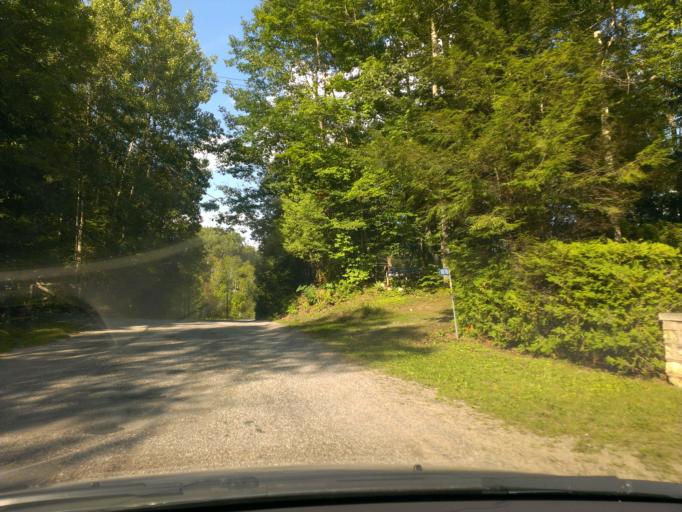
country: CA
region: Ontario
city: Skatepark
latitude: 44.7346
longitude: -76.9163
